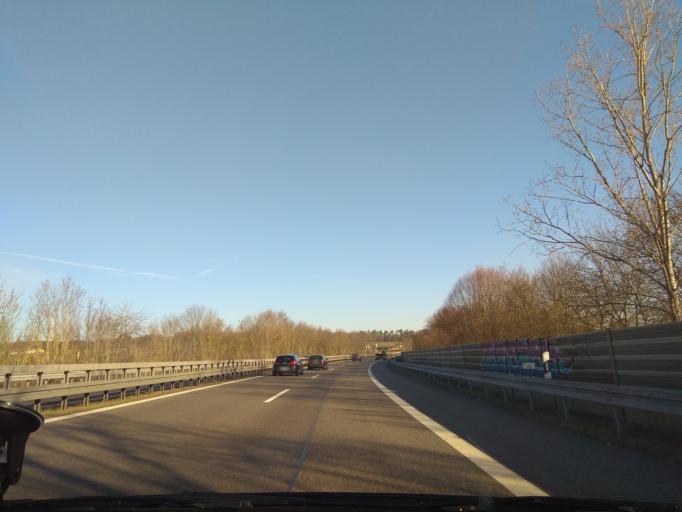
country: DE
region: Baden-Wuerttemberg
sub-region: Tuebingen Region
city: Pliezhausen
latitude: 48.5883
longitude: 9.1696
